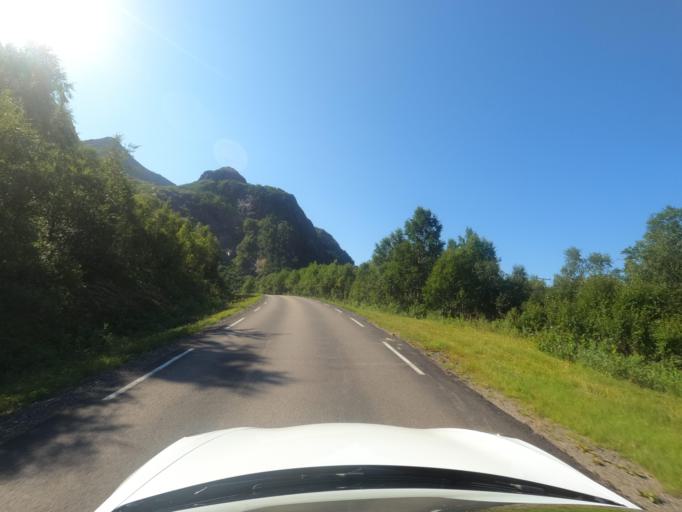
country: NO
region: Nordland
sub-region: Hadsel
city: Stokmarknes
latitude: 68.3418
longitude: 15.0492
